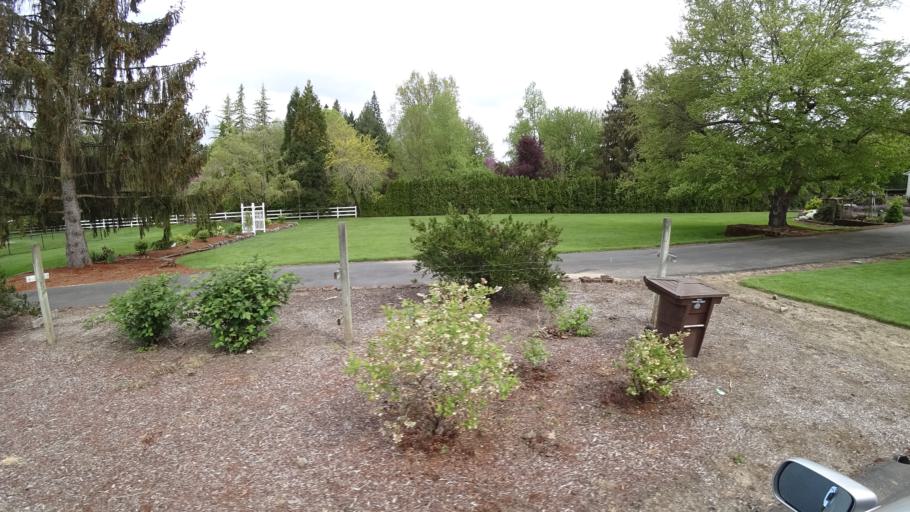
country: US
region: Oregon
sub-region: Washington County
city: Hillsboro
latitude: 45.5290
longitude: -123.0021
